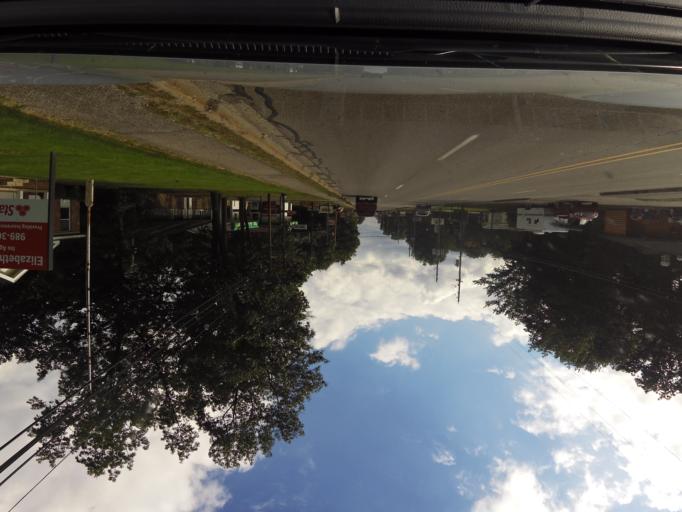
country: US
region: Michigan
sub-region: Roscommon County
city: Prudenville
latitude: 44.2986
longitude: -84.6687
